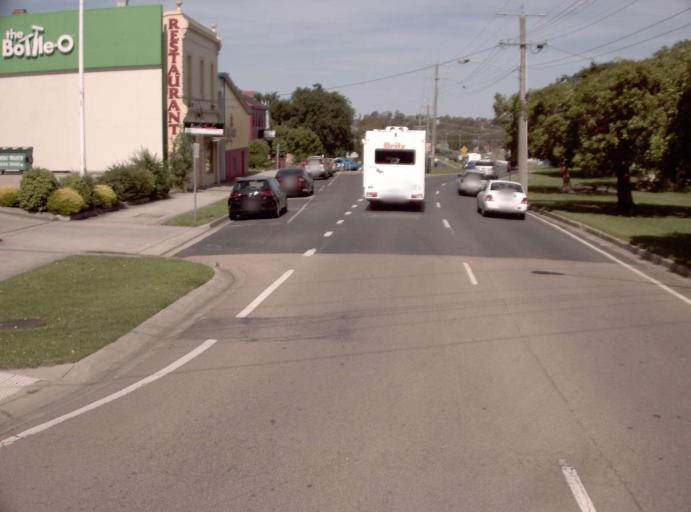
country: AU
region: Victoria
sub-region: East Gippsland
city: Bairnsdale
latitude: -37.8252
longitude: 147.6346
